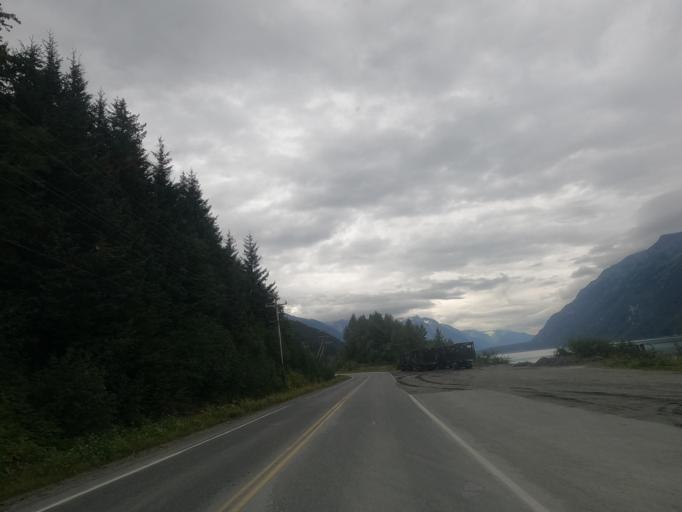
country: US
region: Alaska
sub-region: Haines Borough
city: Haines
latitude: 59.2823
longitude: -135.4681
